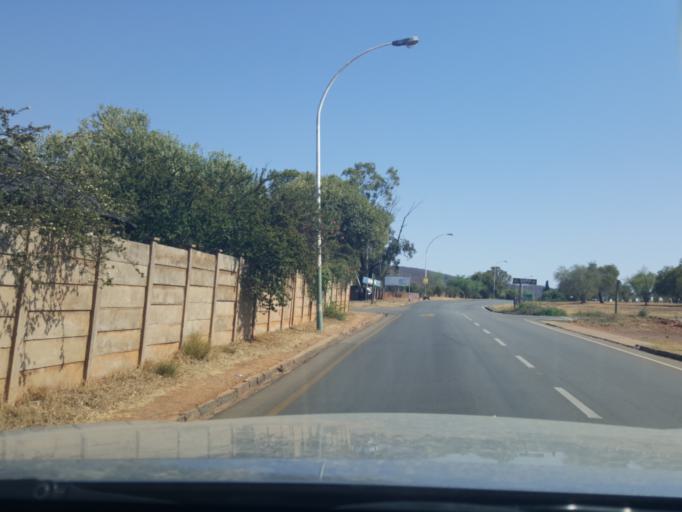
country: ZA
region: North-West
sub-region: Ngaka Modiri Molema District Municipality
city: Zeerust
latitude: -25.5398
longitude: 26.0775
